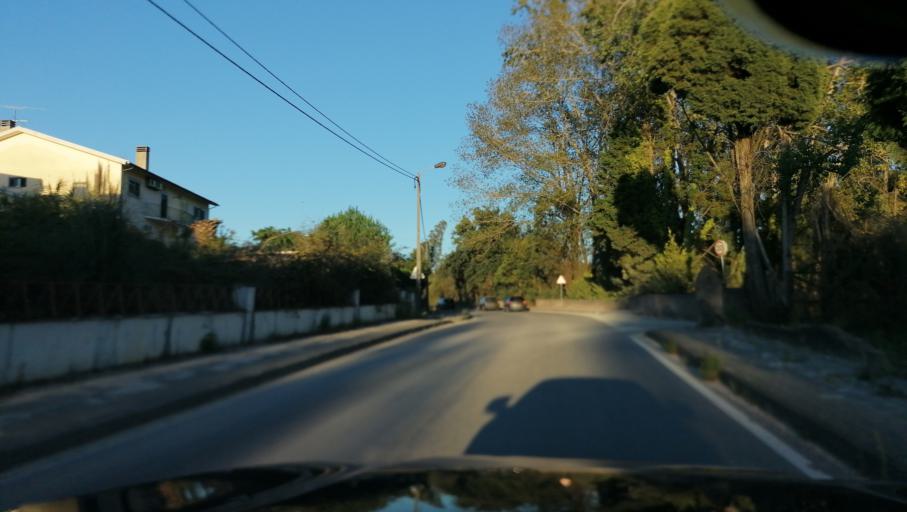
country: PT
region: Aveiro
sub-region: Agueda
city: Agueda
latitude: 40.5569
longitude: -8.4772
